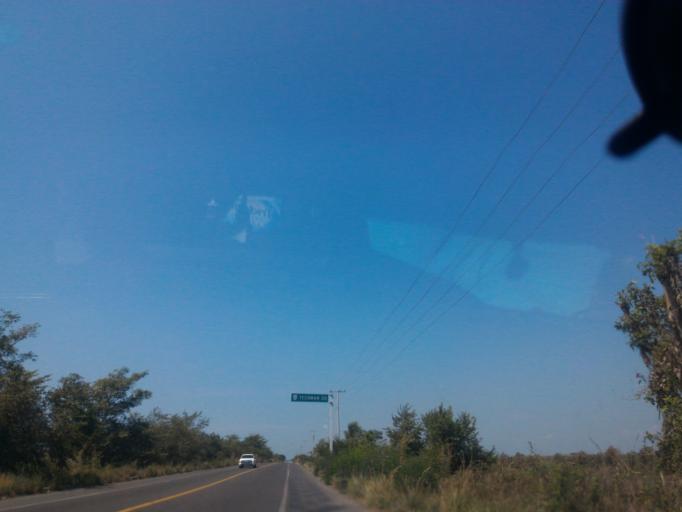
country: MX
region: Michoacan
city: Coahuayana Viejo
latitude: 18.7736
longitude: -103.7449
